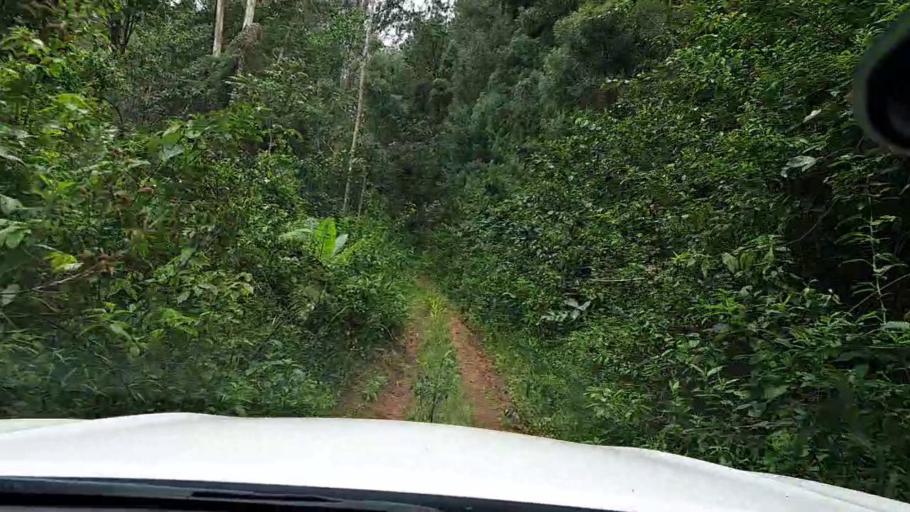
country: RW
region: Western Province
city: Kibuye
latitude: -2.2902
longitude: 29.3052
